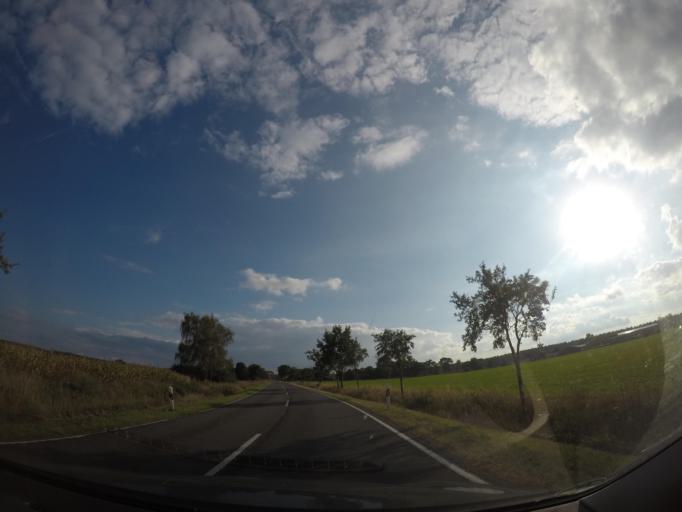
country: DE
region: Saxony-Anhalt
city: Weferlingen
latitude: 52.3726
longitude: 11.0977
